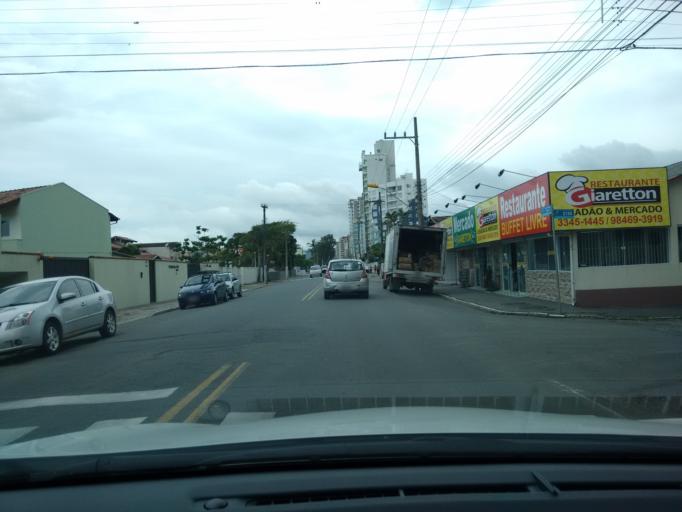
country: BR
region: Santa Catarina
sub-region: Penha
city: Penha
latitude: -26.7504
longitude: -48.6779
